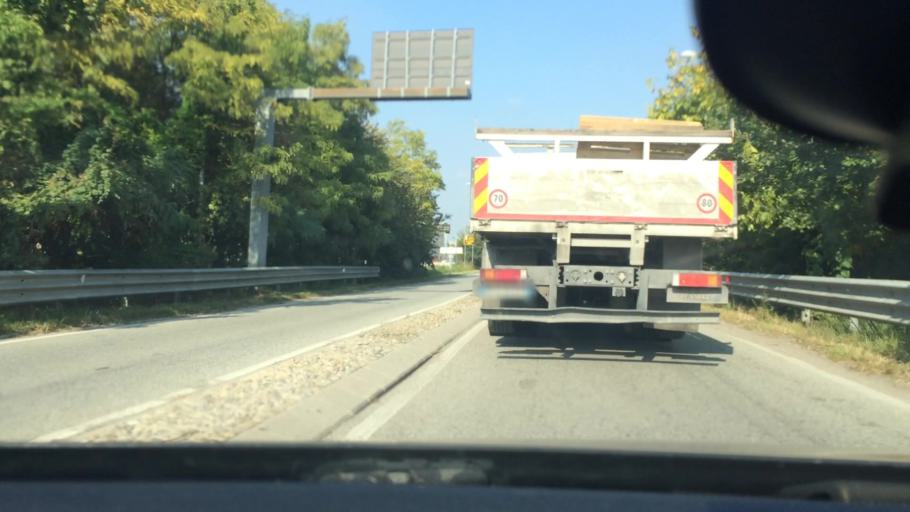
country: IT
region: Lombardy
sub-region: Citta metropolitana di Milano
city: Arluno
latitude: 45.4953
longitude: 8.9347
